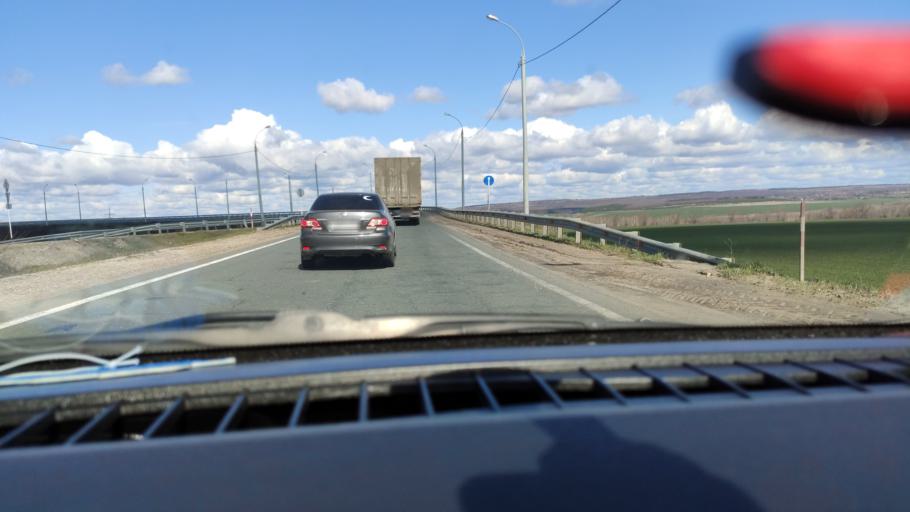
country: RU
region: Samara
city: Varlamovo
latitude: 53.1977
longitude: 48.2923
